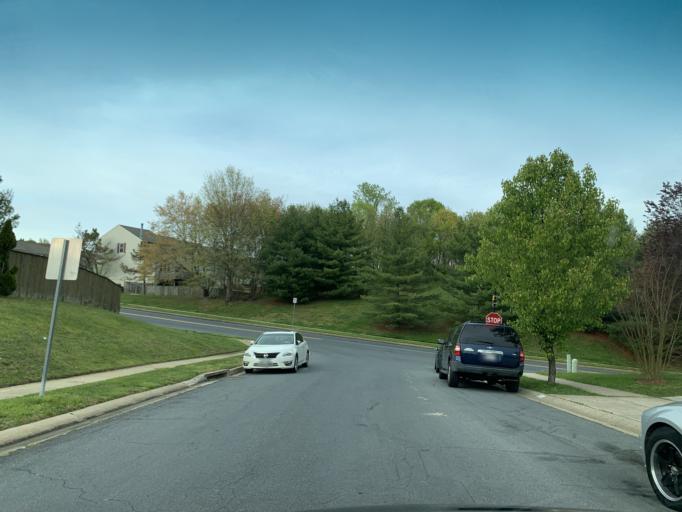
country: US
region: Maryland
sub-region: Harford County
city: Riverside
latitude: 39.4766
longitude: -76.2541
